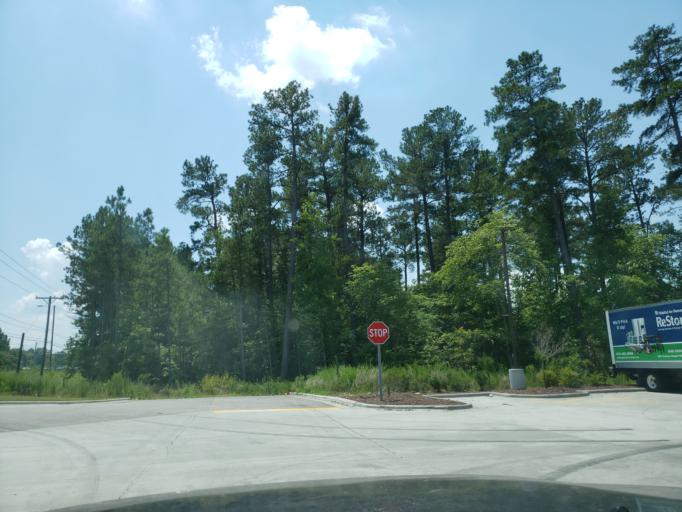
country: US
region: North Carolina
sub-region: Orange County
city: Chapel Hill
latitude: 35.9071
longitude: -78.9607
